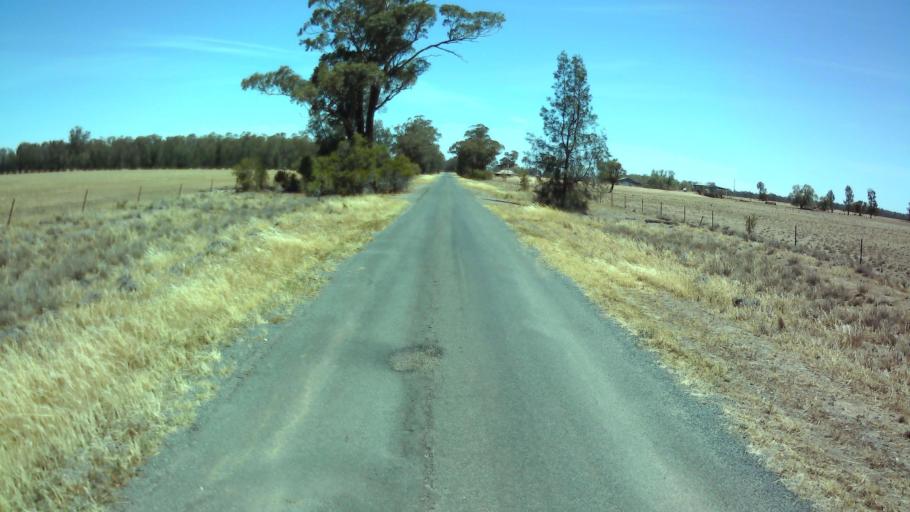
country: AU
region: New South Wales
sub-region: Weddin
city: Grenfell
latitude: -33.9007
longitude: 147.6864
